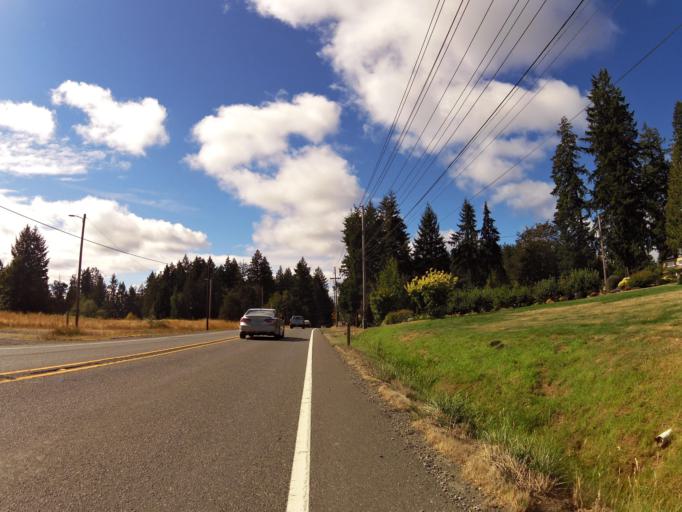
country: US
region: Washington
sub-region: Mason County
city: Shelton
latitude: 47.2501
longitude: -123.0431
